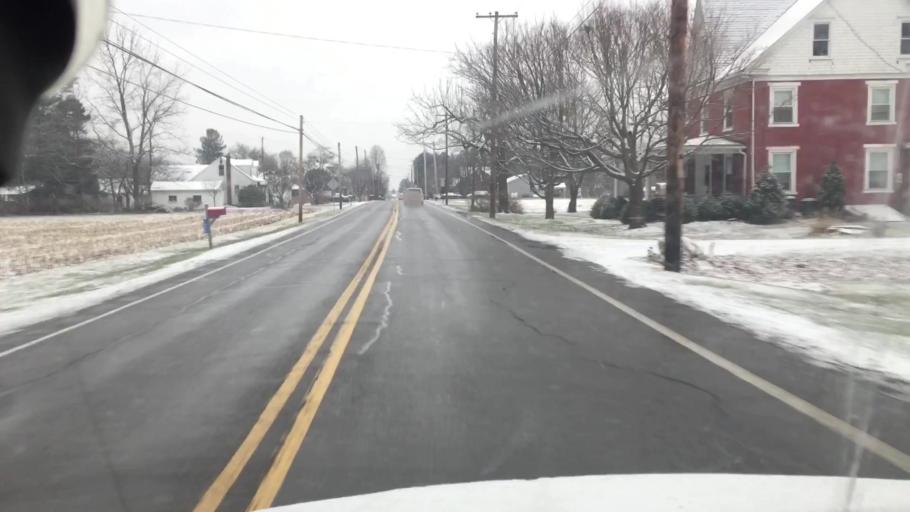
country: US
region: Pennsylvania
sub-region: Luzerne County
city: Nescopeck
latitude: 41.0545
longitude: -76.2035
